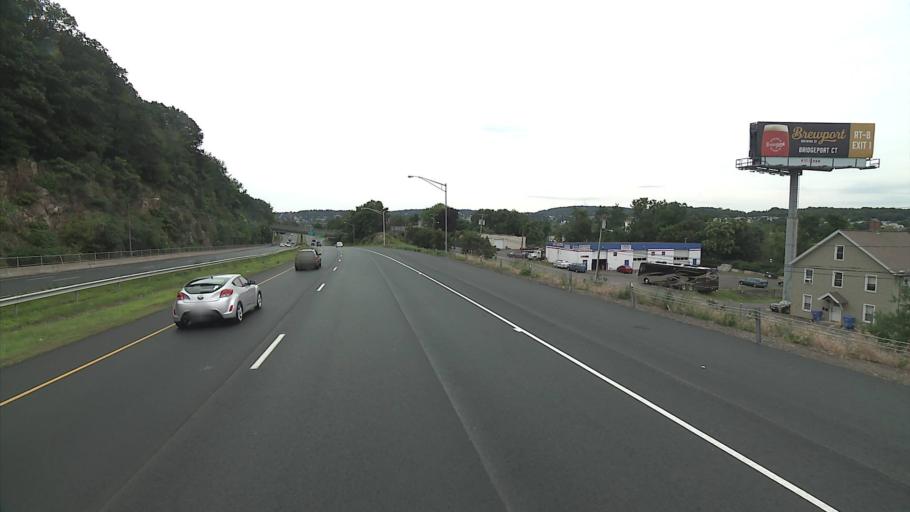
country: US
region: Connecticut
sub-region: New Haven County
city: Waterbury
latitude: 41.5343
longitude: -73.0436
